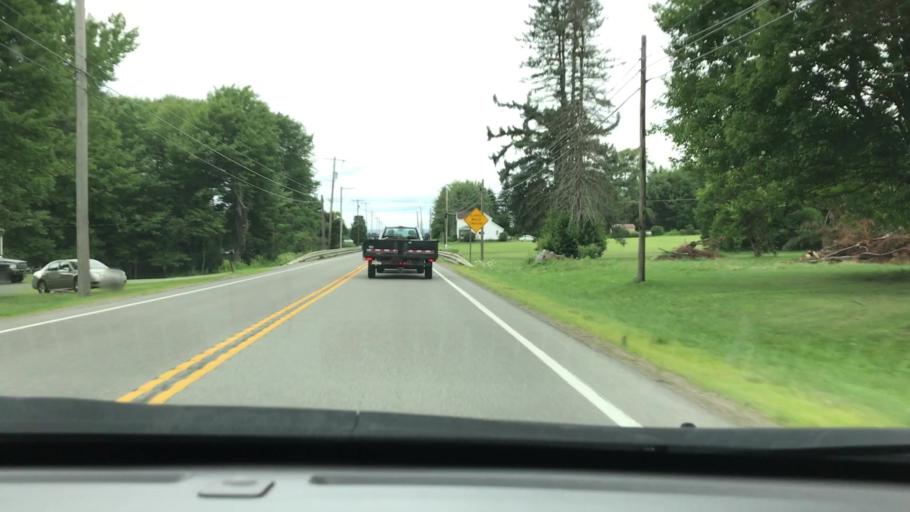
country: US
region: Pennsylvania
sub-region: Elk County
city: Ridgway
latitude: 41.3997
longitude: -78.7007
